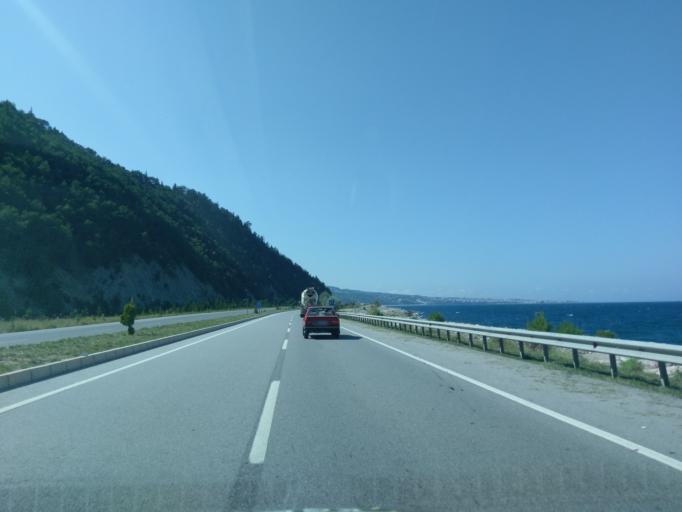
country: TR
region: Sinop
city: Gerze
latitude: 41.7467
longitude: 35.2450
